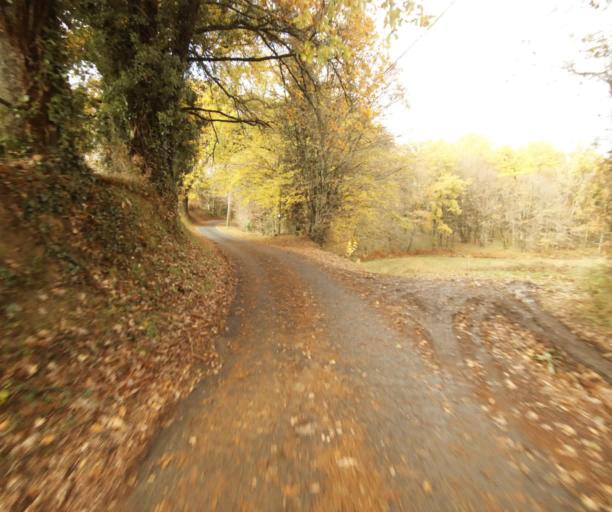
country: FR
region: Limousin
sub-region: Departement de la Correze
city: Sainte-Fereole
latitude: 45.2117
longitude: 1.6247
